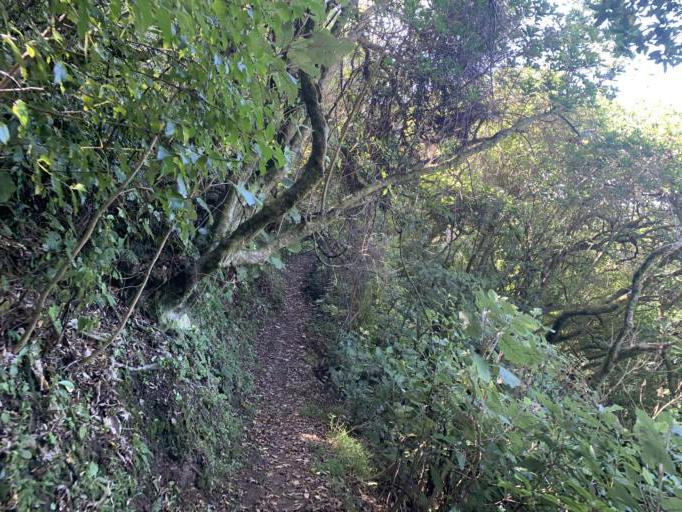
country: NZ
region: Wellington
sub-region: Wellington City
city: Kelburn
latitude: -41.2976
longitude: 174.7551
